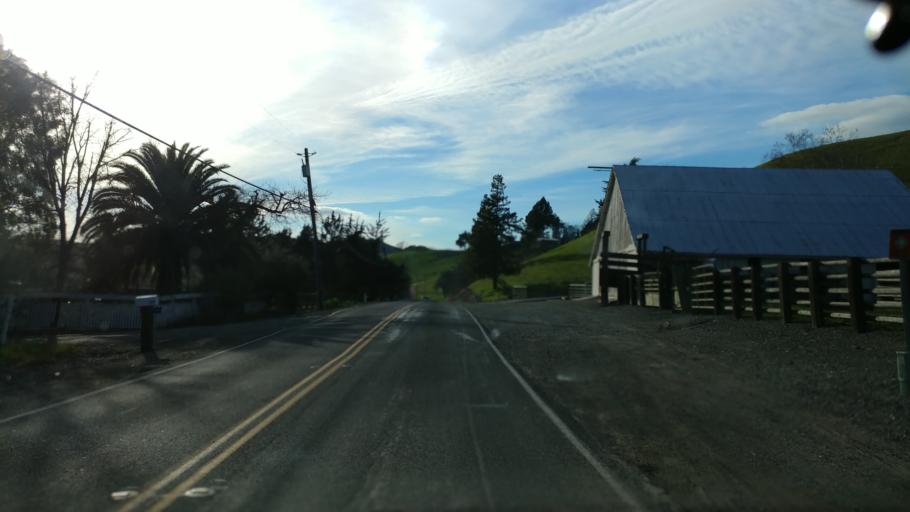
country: US
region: California
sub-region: Contra Costa County
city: Blackhawk
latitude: 37.7763
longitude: -121.8540
